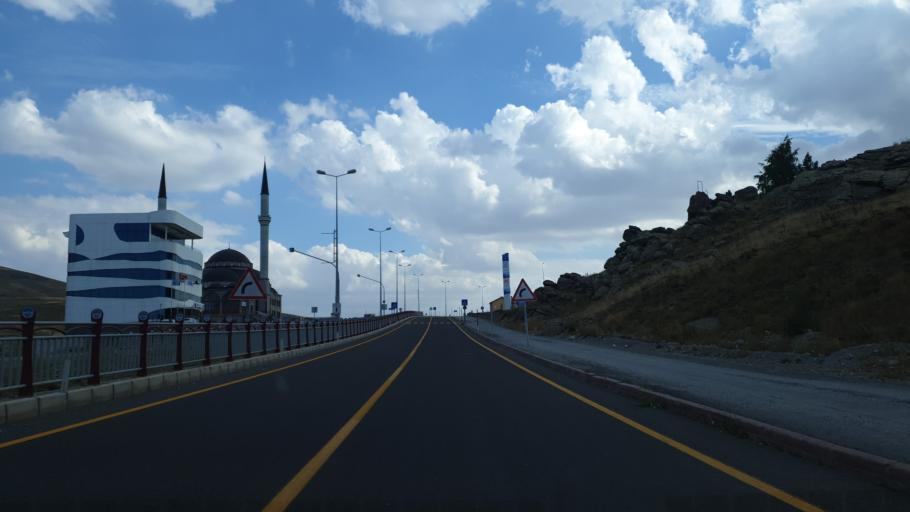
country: TR
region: Kayseri
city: Hacilar
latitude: 38.5424
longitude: 35.5273
